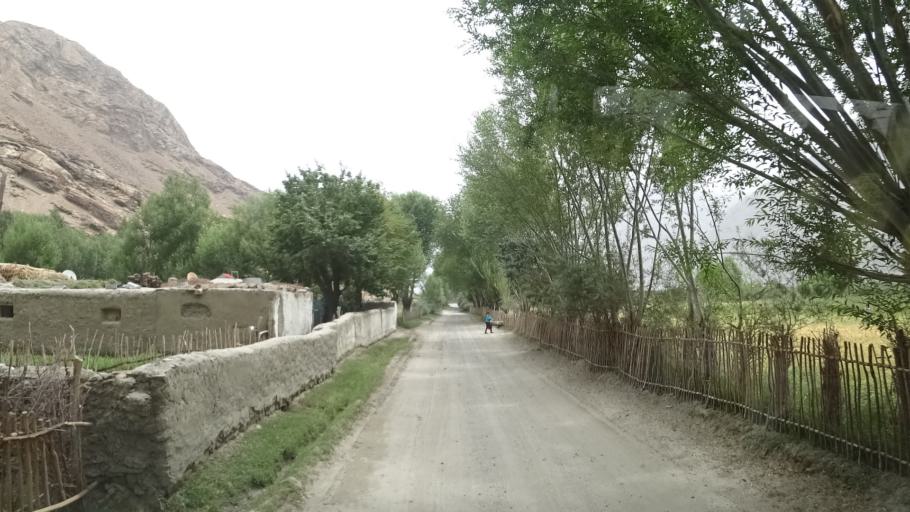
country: AF
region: Badakhshan
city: Khandud
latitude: 37.0220
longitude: 72.5942
